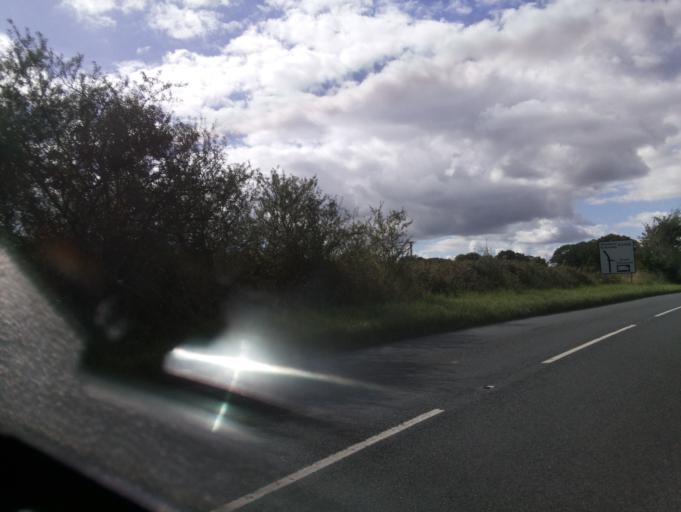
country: GB
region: England
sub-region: Wiltshire
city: Erlestoke
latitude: 51.2814
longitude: -2.0319
